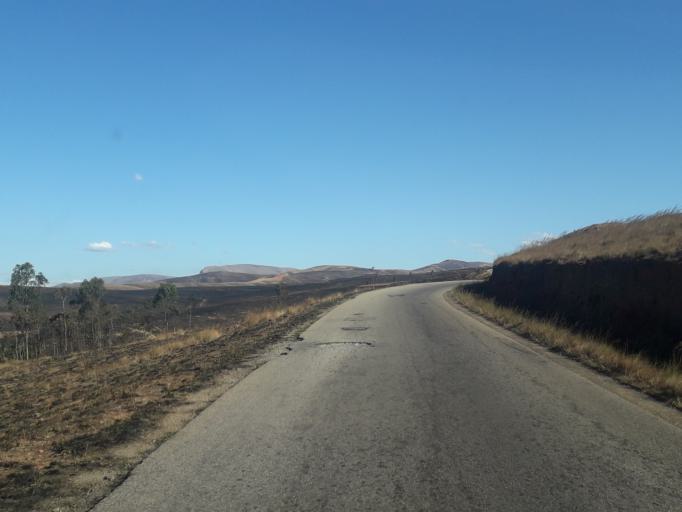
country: MG
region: Analamanga
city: Ankazobe
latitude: -17.7650
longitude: 47.0176
